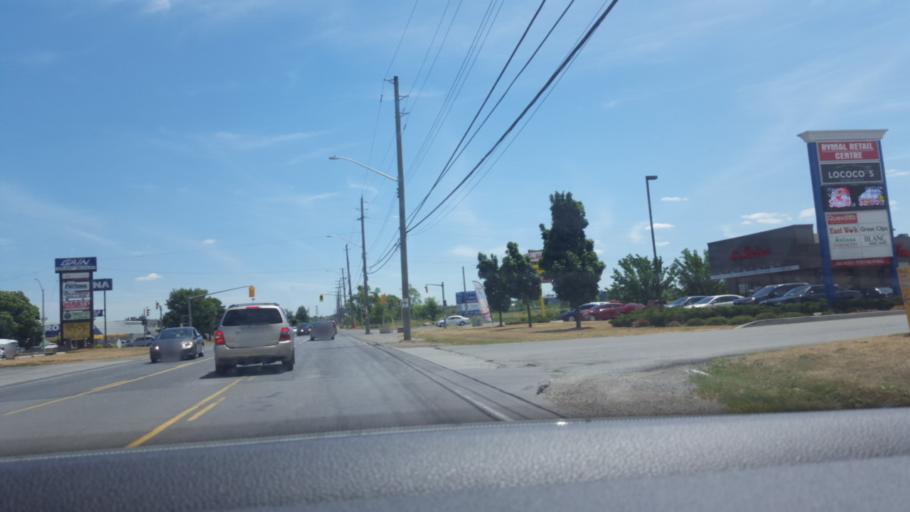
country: CA
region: Ontario
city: Hamilton
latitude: 43.1911
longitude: -79.8466
